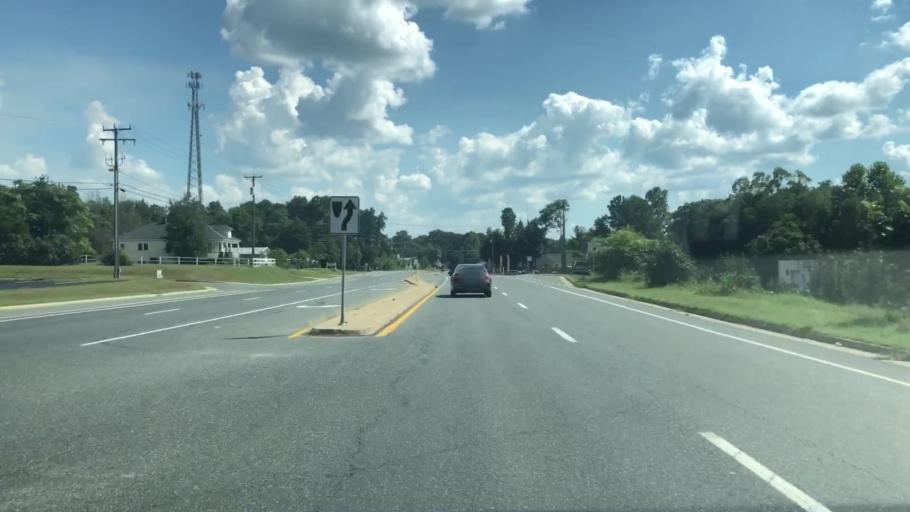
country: US
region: Virginia
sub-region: City of Fredericksburg
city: Fredericksburg
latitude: 38.3100
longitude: -77.4456
